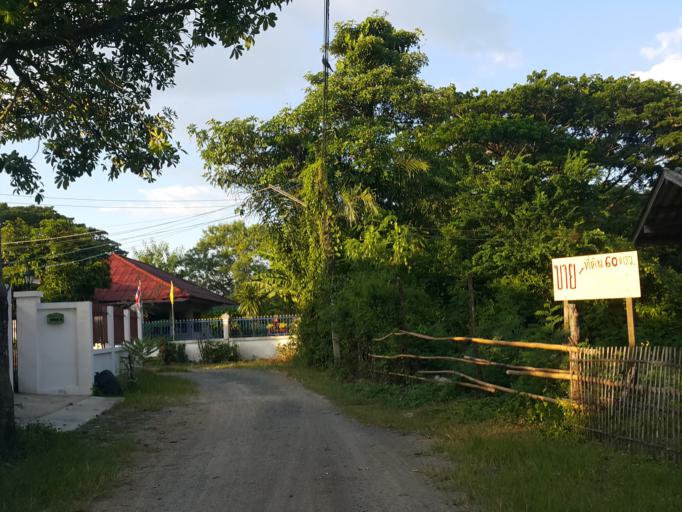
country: TH
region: Chiang Mai
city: San Kamphaeng
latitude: 18.7488
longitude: 99.1189
